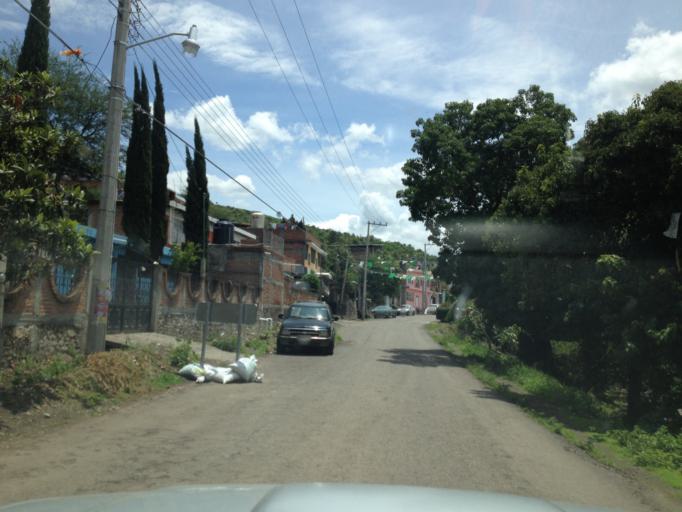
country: MX
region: Michoacan
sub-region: Tarimbaro
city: El Colegio
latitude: 19.7730
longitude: -101.1745
